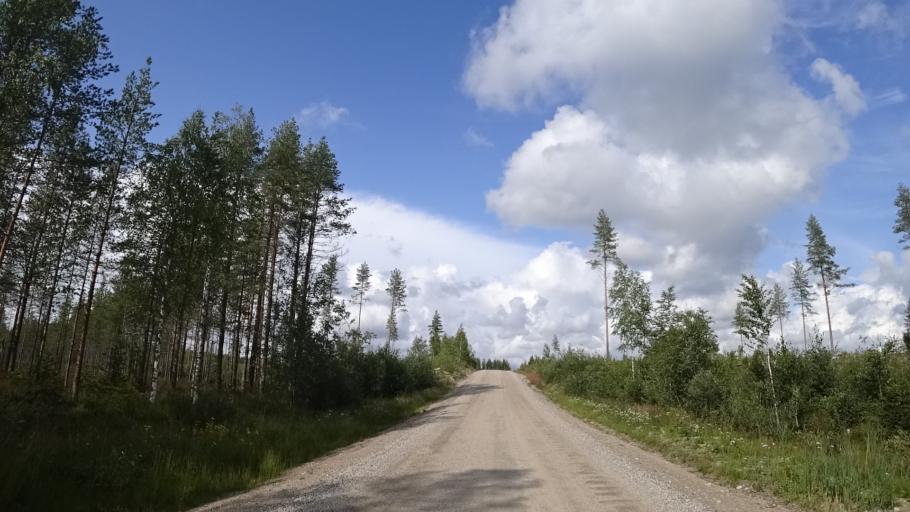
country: FI
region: North Karelia
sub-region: Pielisen Karjala
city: Lieksa
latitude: 63.5836
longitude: 30.1331
